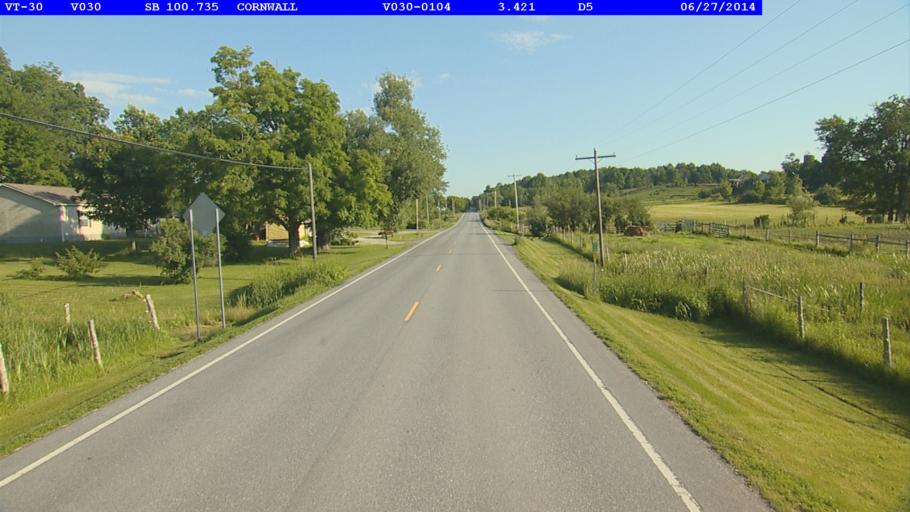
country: US
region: Vermont
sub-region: Addison County
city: Middlebury (village)
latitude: 43.9569
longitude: -73.2099
